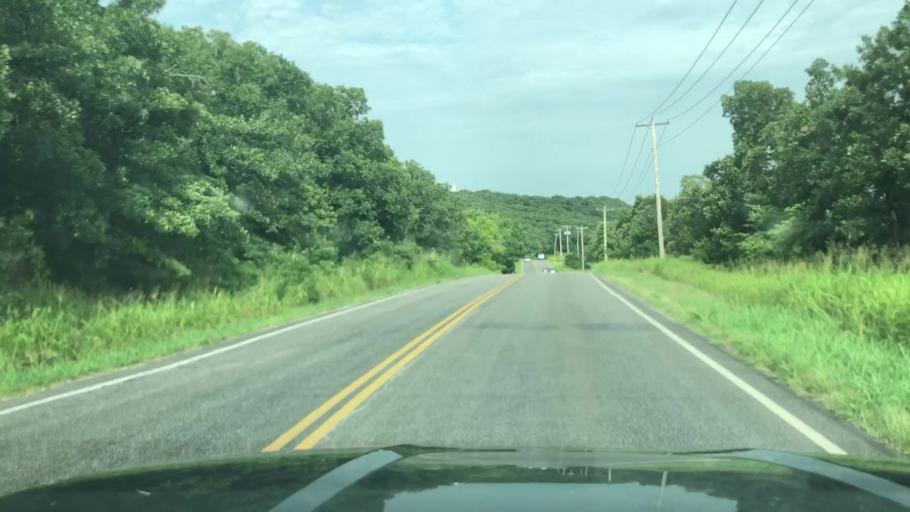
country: US
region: Oklahoma
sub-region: Tulsa County
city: Oakhurst
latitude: 36.0909
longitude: -96.0832
